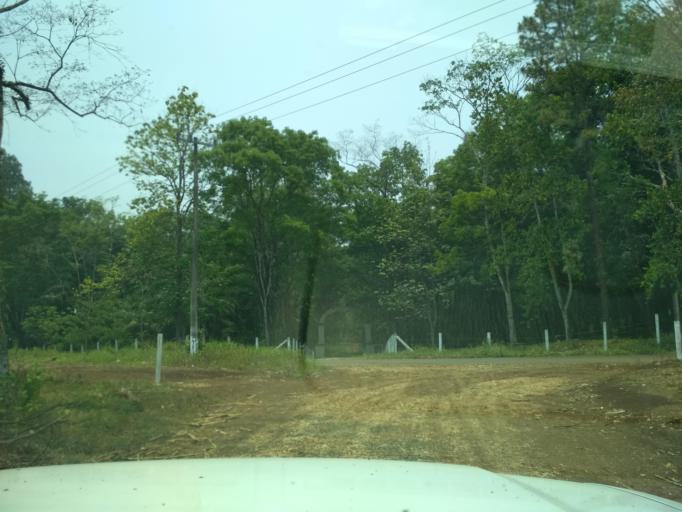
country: MX
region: Veracruz
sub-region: Tezonapa
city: Laguna Chica (Pueblo Nuevo)
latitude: 18.5135
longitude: -96.7580
